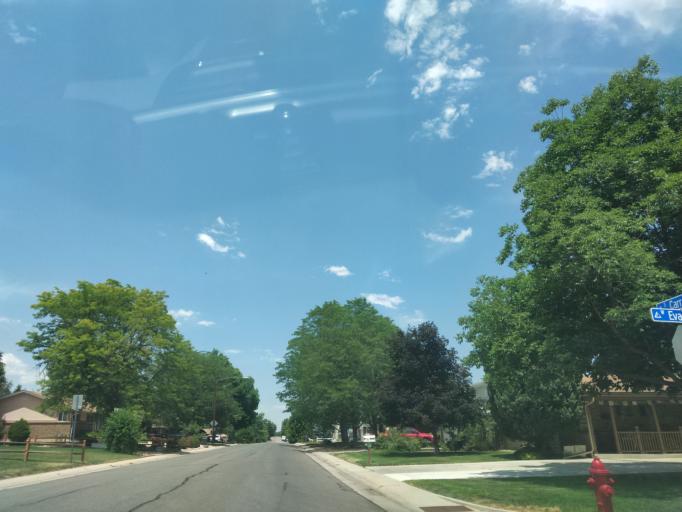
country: US
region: Colorado
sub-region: Jefferson County
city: Lakewood
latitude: 39.6795
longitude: -105.0908
